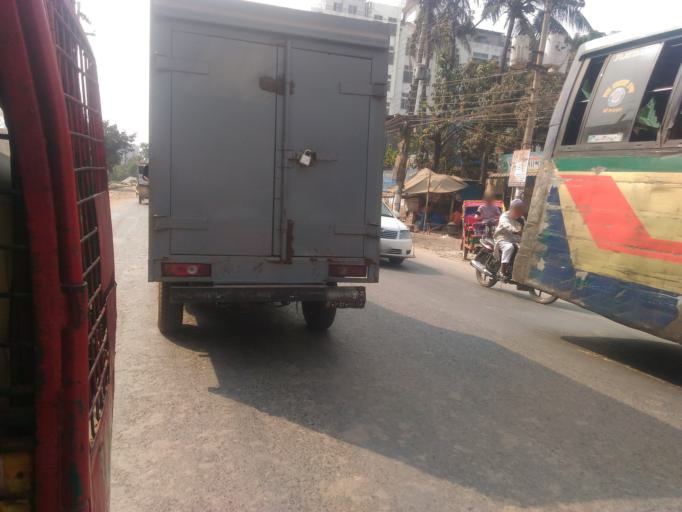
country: BD
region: Dhaka
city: Tungi
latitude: 23.9916
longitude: 90.3946
